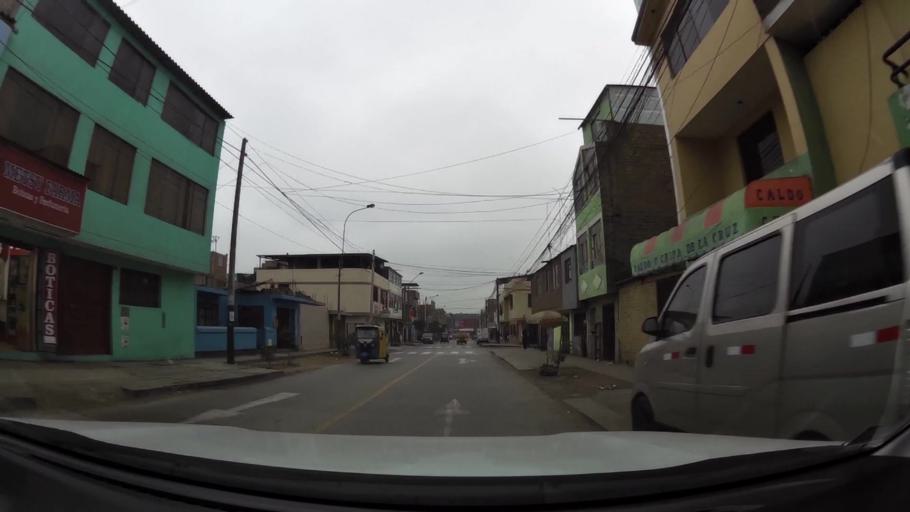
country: PE
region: Lima
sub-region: Lima
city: Surco
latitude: -12.1494
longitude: -76.9762
